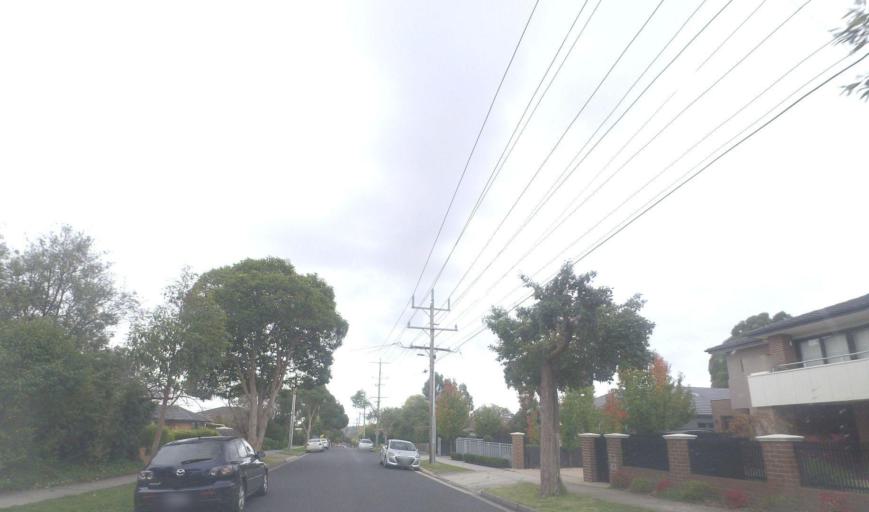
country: AU
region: Victoria
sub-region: Whitehorse
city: Blackburn North
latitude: -37.8088
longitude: 145.1524
